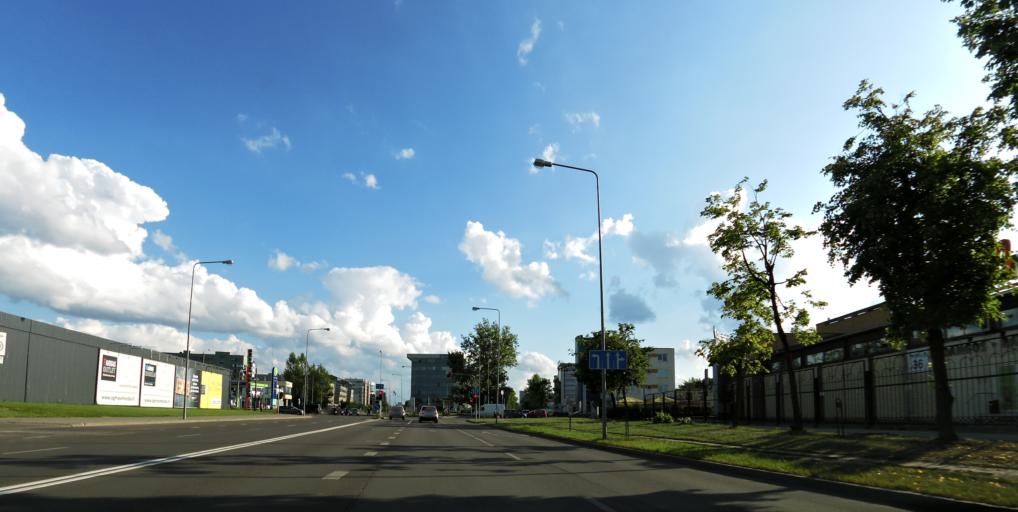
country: LT
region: Vilnius County
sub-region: Vilnius
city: Vilnius
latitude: 54.7131
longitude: 25.2929
